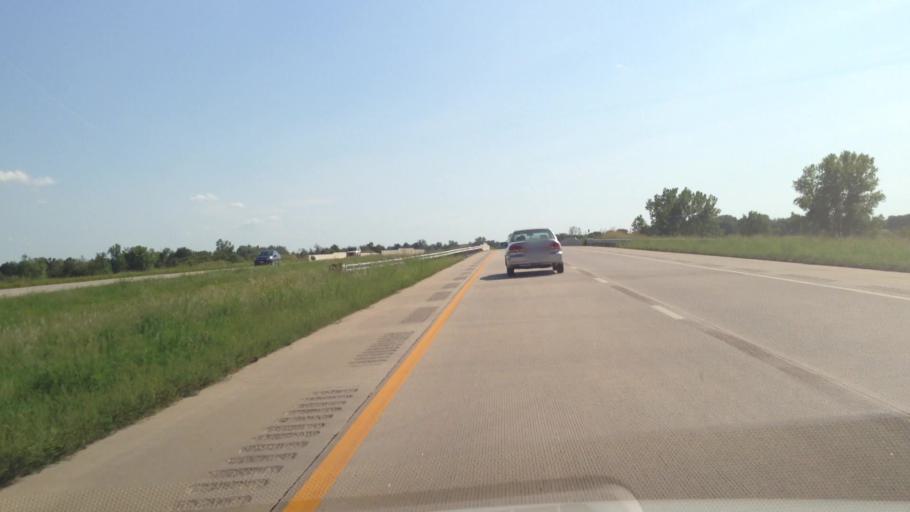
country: US
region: Kansas
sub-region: Bourbon County
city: Fort Scott
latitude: 37.9694
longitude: -94.7054
